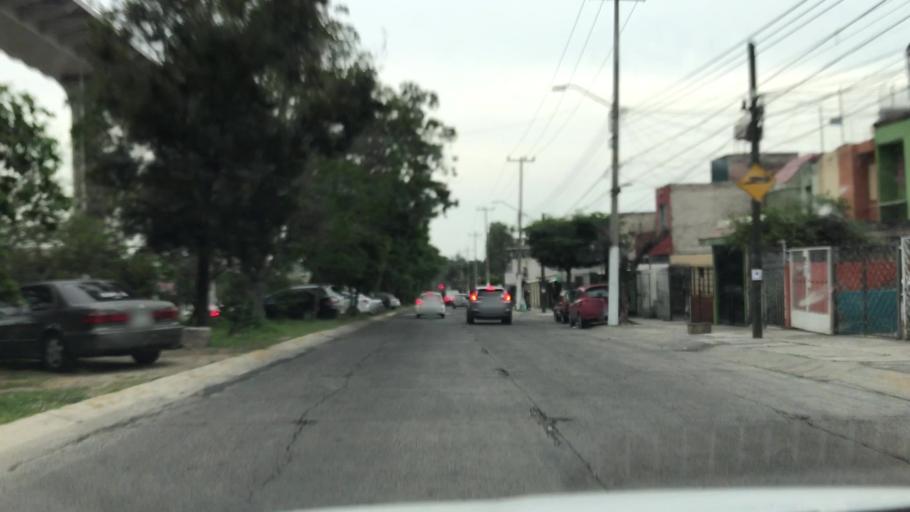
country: MX
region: Jalisco
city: Zapopan2
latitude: 20.7406
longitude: -103.4070
